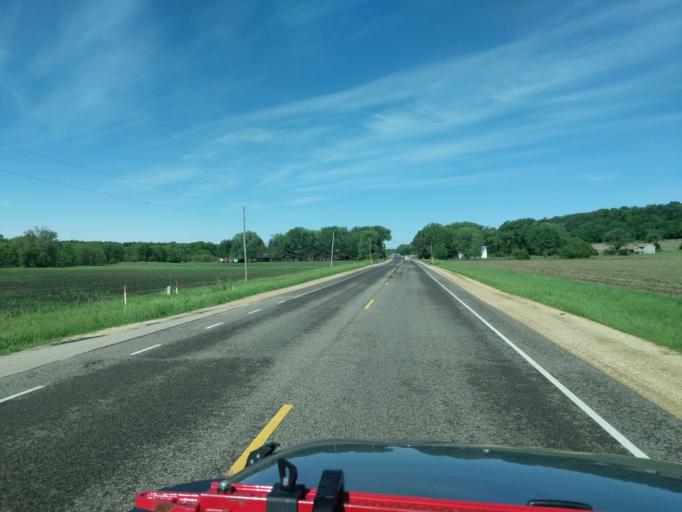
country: US
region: Wisconsin
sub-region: Pierce County
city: River Falls
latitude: 44.8509
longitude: -92.5835
